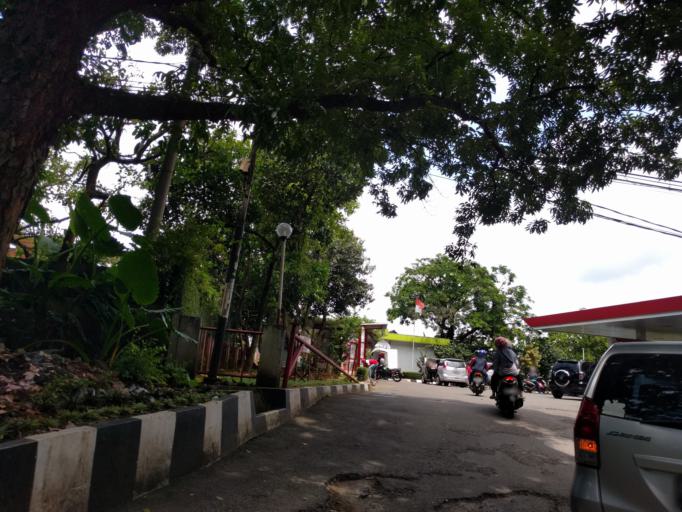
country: ID
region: West Java
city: Bogor
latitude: -6.6130
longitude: 106.8131
